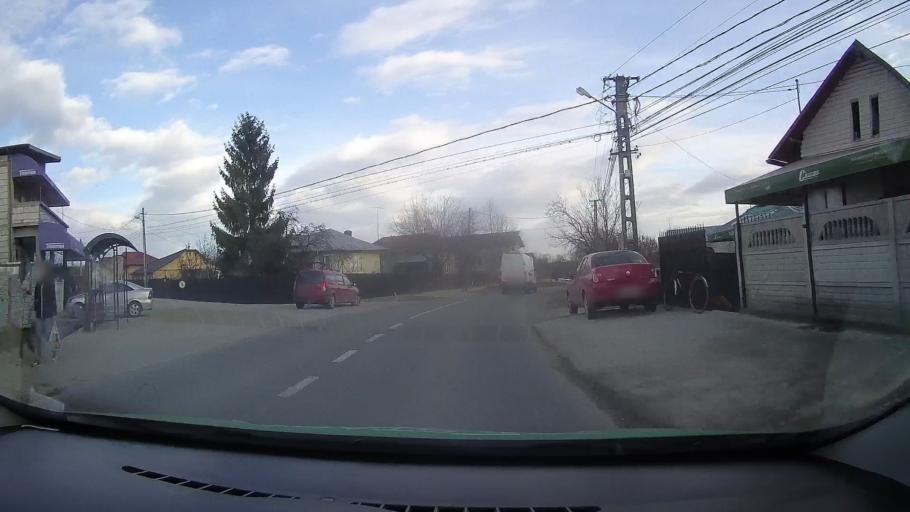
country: RO
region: Dambovita
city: Razvad
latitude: 44.9351
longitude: 25.5387
